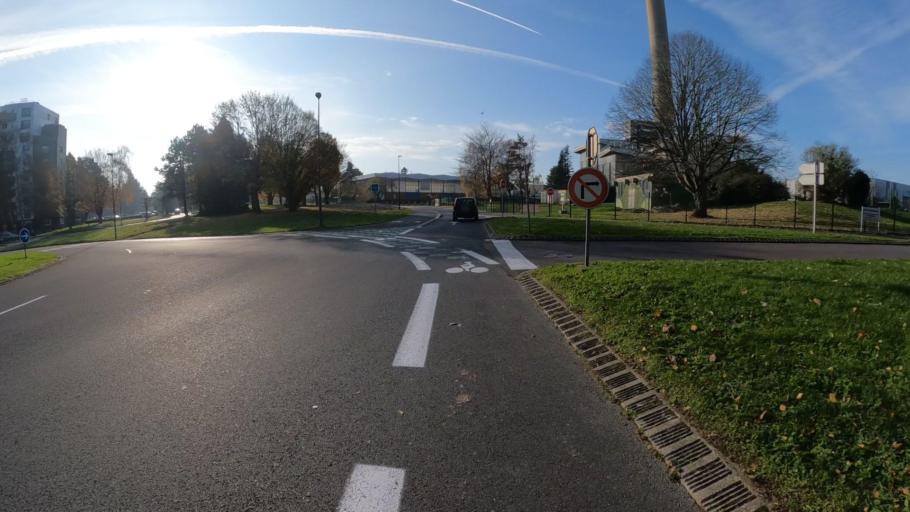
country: FR
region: Lower Normandy
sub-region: Departement du Calvados
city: Herouville-Saint-Clair
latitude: 49.2093
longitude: -0.3344
